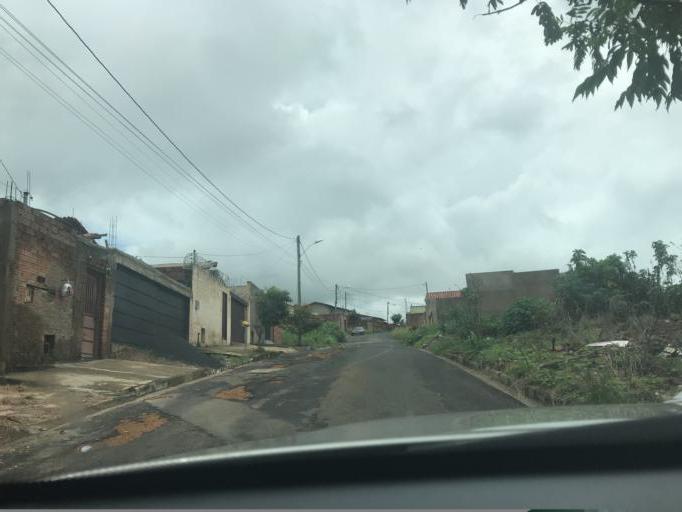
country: BR
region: Minas Gerais
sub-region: Araxa
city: Araxa
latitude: -19.5775
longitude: -46.9309
